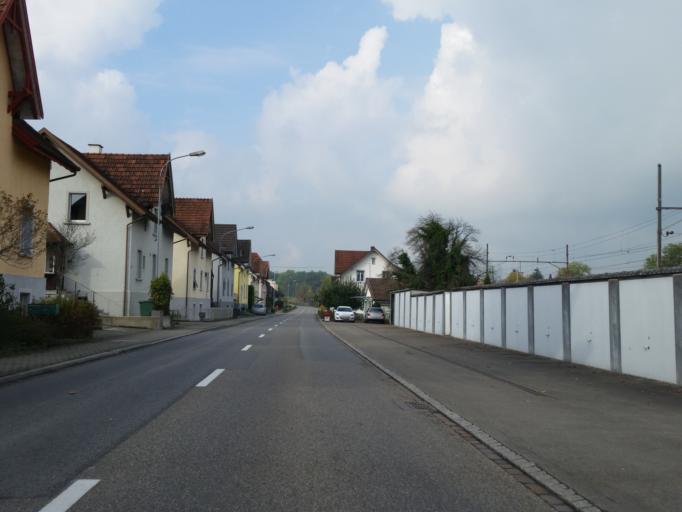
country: CH
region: Thurgau
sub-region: Arbon District
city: Amriswil
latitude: 47.5511
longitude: 9.2930
